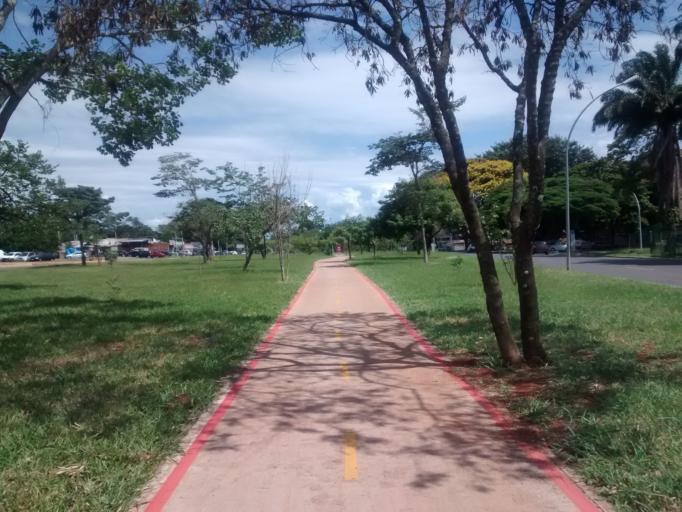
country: BR
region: Federal District
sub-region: Brasilia
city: Brasilia
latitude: -15.7764
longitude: -47.8911
